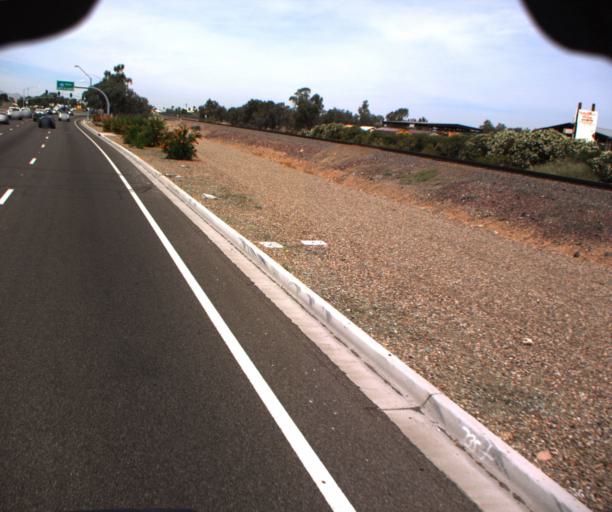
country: US
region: Arizona
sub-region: Maricopa County
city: Sun City
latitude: 33.5934
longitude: -112.2577
